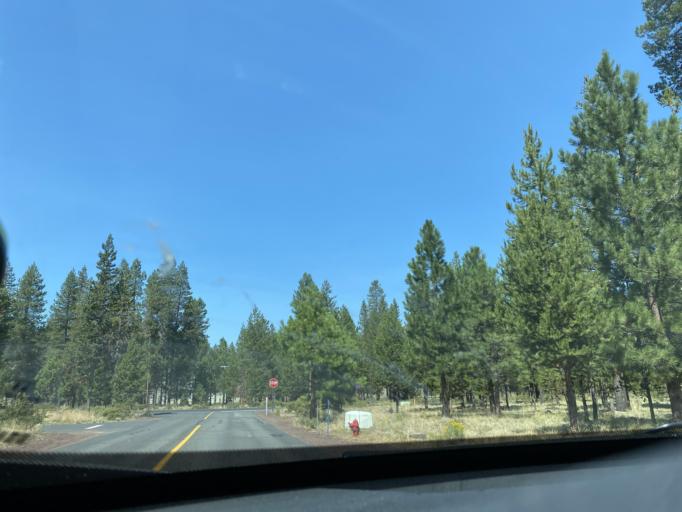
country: US
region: Oregon
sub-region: Deschutes County
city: Sunriver
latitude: 43.8932
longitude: -121.4215
